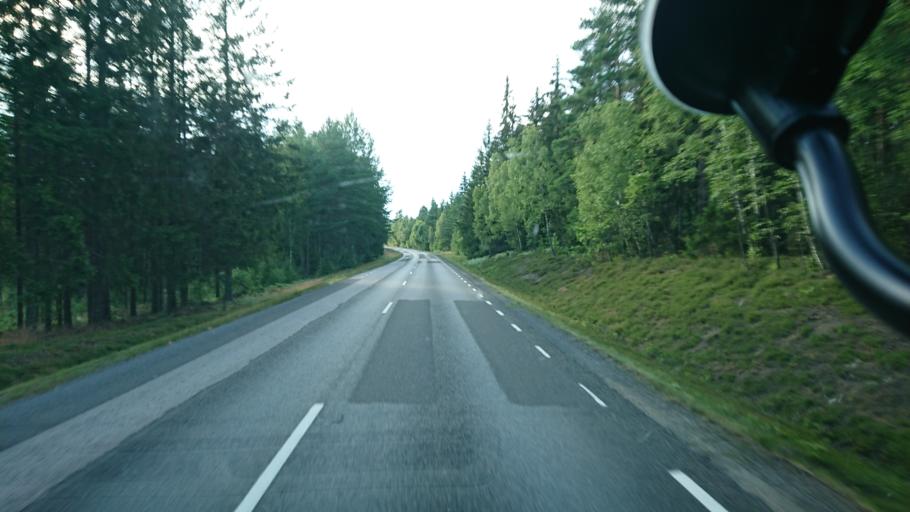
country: SE
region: Kronoberg
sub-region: Vaxjo Kommun
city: Rottne
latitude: 57.0285
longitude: 14.9762
